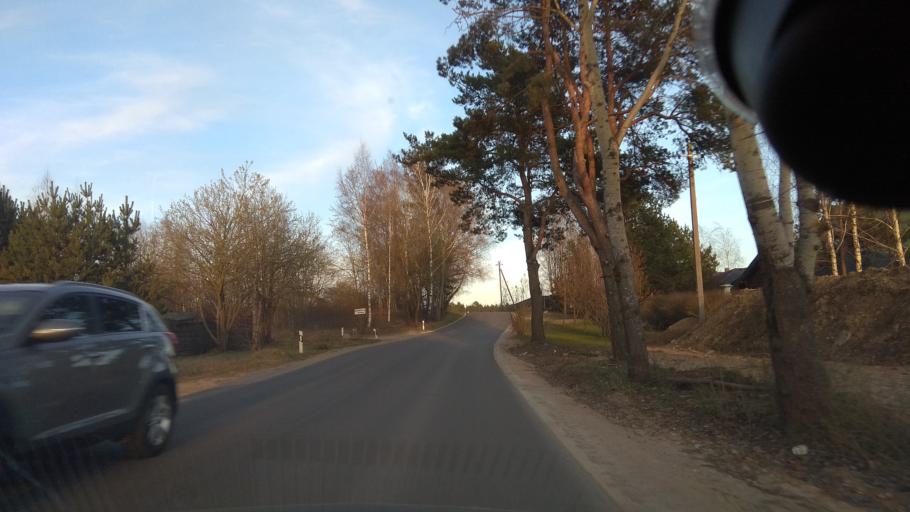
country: LT
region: Vilnius County
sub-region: Vilnius
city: Fabijoniskes
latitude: 54.7574
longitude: 25.2325
